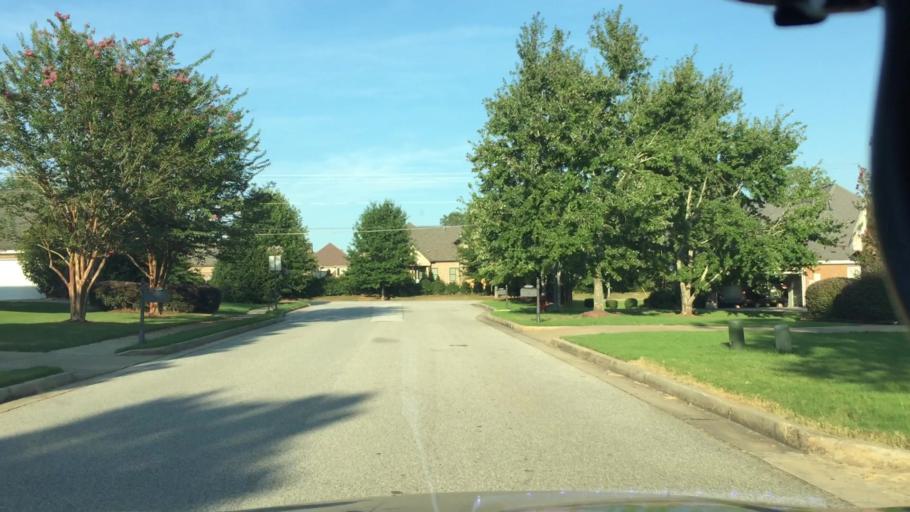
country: US
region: Alabama
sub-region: Lee County
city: Auburn
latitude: 32.5730
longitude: -85.4396
